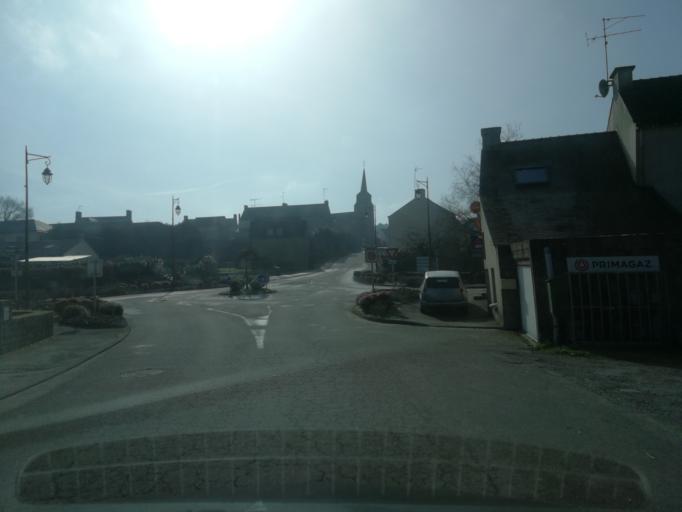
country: FR
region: Brittany
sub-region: Departement du Morbihan
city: La Vraie-Croix
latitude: 47.7136
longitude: -2.5155
